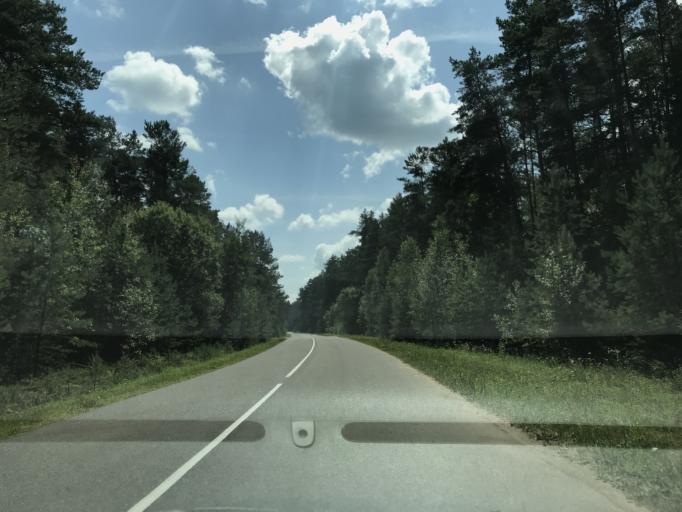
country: BY
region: Minsk
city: Rakaw
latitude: 54.0007
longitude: 26.9855
